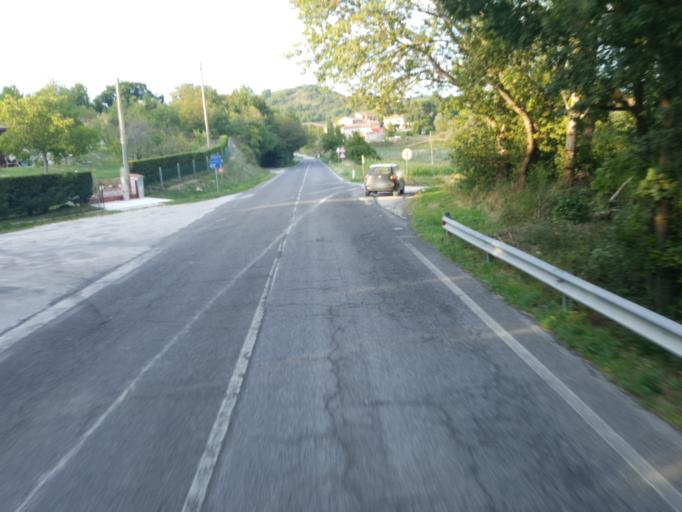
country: IT
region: The Marches
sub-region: Provincia di Ancona
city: Fabriano
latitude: 43.3455
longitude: 12.8289
